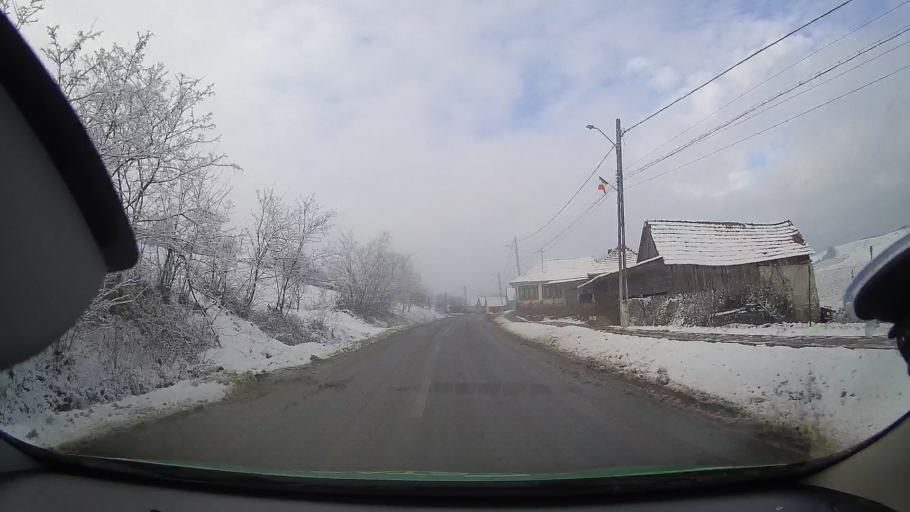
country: RO
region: Mures
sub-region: Comuna Atintis
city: Atintis
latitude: 46.4313
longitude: 24.1038
